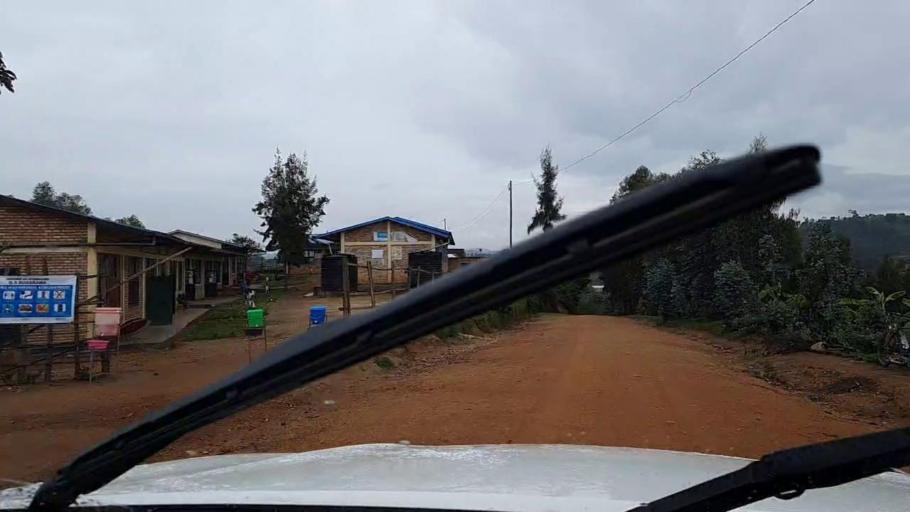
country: RW
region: Southern Province
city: Nzega
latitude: -2.4658
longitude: 29.4962
